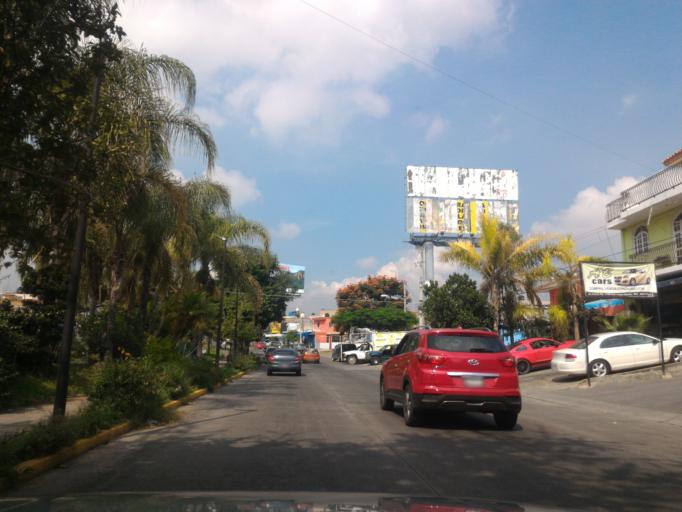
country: MX
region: Jalisco
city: Guadalajara
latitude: 20.6288
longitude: -103.4000
